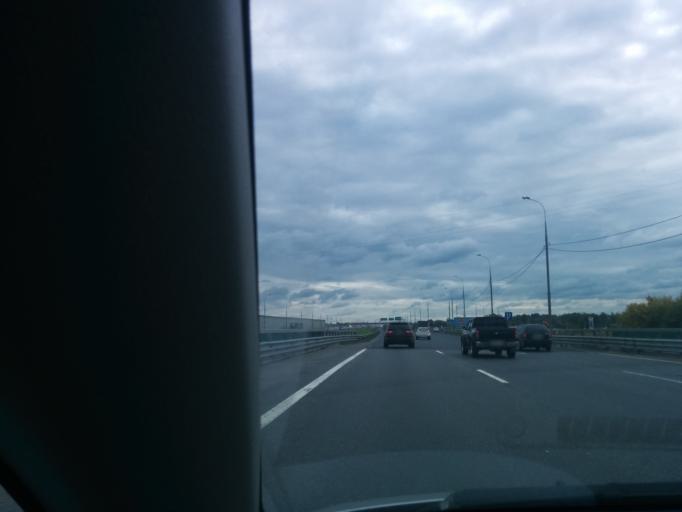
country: RU
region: Moskovskaya
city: Yam
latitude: 55.4868
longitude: 37.7396
